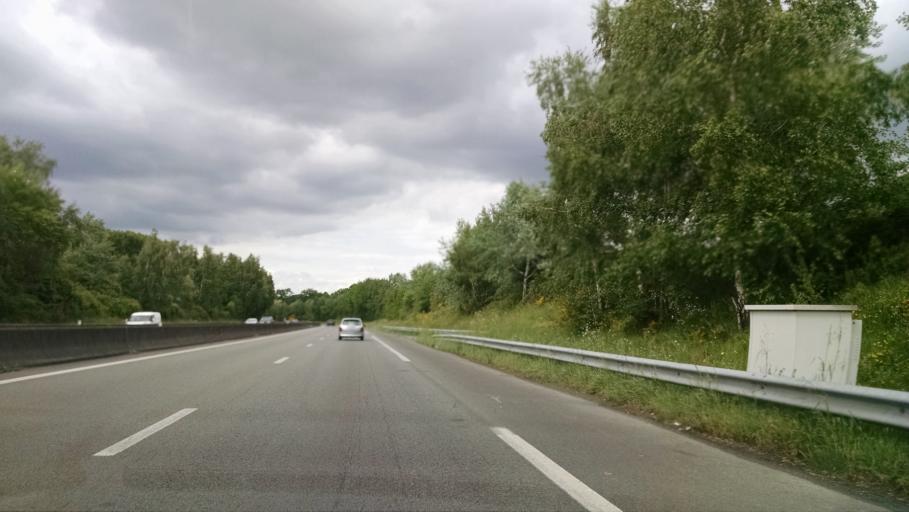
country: FR
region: Pays de la Loire
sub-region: Departement de la Loire-Atlantique
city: Basse-Goulaine
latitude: 47.2031
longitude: -1.4837
